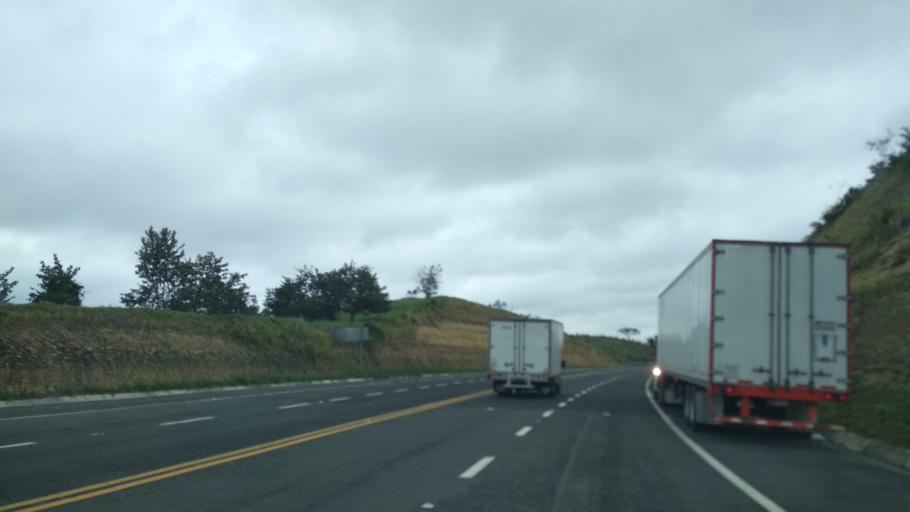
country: MX
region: Veracruz
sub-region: Papantla
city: Polutla
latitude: 20.4582
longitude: -97.2454
